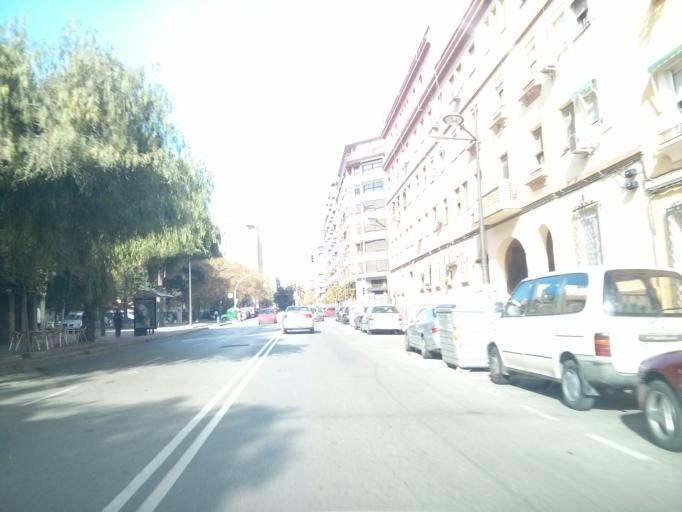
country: ES
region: Valencia
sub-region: Provincia de Valencia
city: Valencia
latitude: 39.4827
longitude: -0.3847
